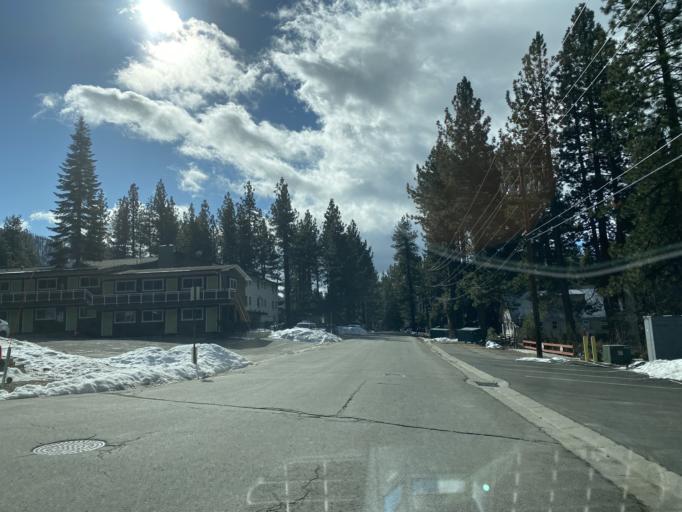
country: US
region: Nevada
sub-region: Douglas County
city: Kingsbury
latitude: 38.9591
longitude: -119.9458
